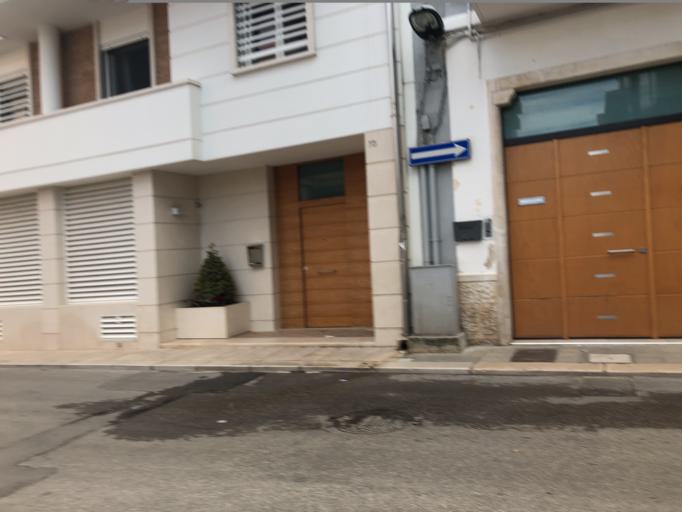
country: IT
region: Apulia
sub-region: Provincia di Bari
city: Bitonto
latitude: 41.1127
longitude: 16.6894
